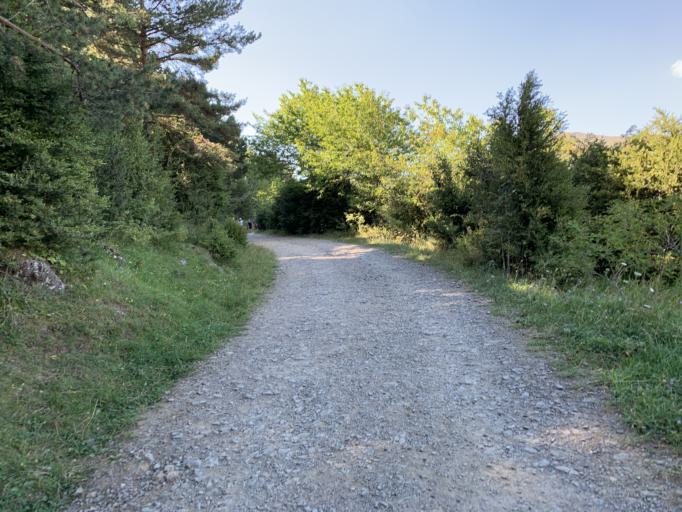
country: ES
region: Aragon
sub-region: Provincia de Huesca
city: Hoz de Jaca
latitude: 42.6993
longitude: -0.3350
